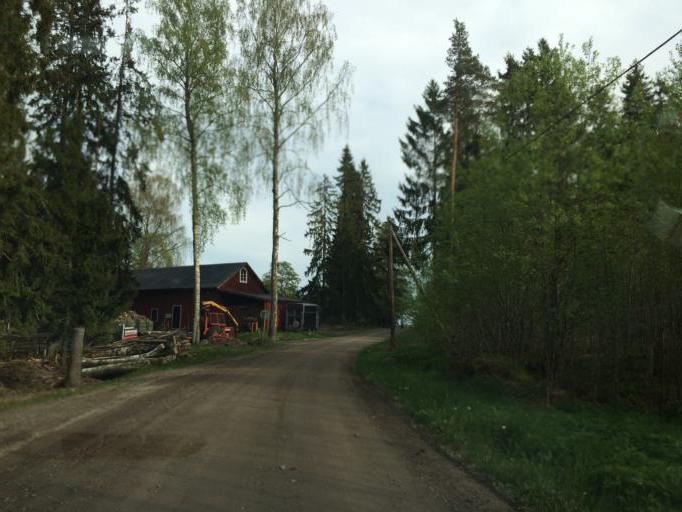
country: SE
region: Vaestmanland
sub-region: Hallstahammars Kommun
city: Hallstahammar
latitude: 59.6022
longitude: 16.0991
